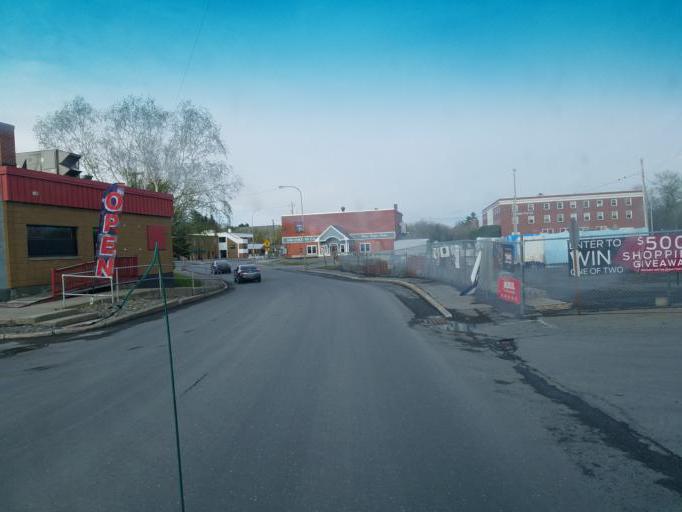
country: US
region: Maine
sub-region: Aroostook County
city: Caribou
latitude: 46.8594
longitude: -68.0143
